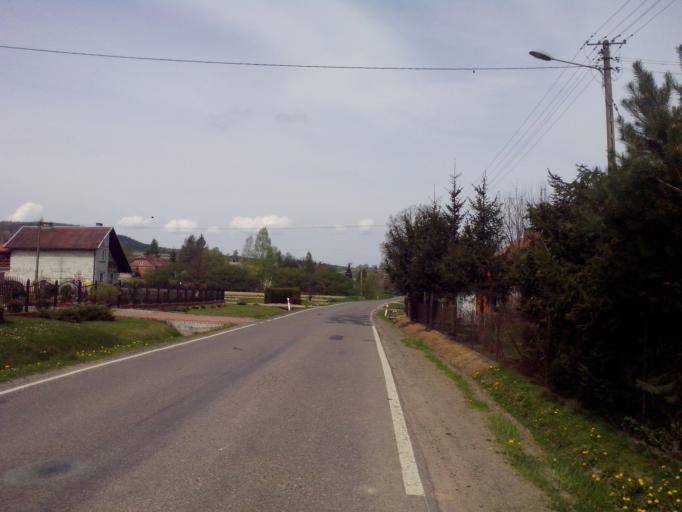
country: PL
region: Subcarpathian Voivodeship
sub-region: Powiat strzyzowski
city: Jawornik
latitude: 49.8097
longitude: 21.8495
